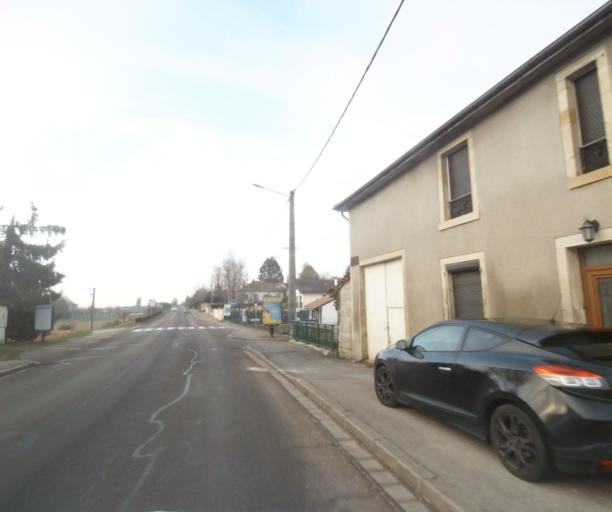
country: FR
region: Champagne-Ardenne
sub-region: Departement de la Haute-Marne
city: Chancenay
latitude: 48.6677
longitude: 4.9836
